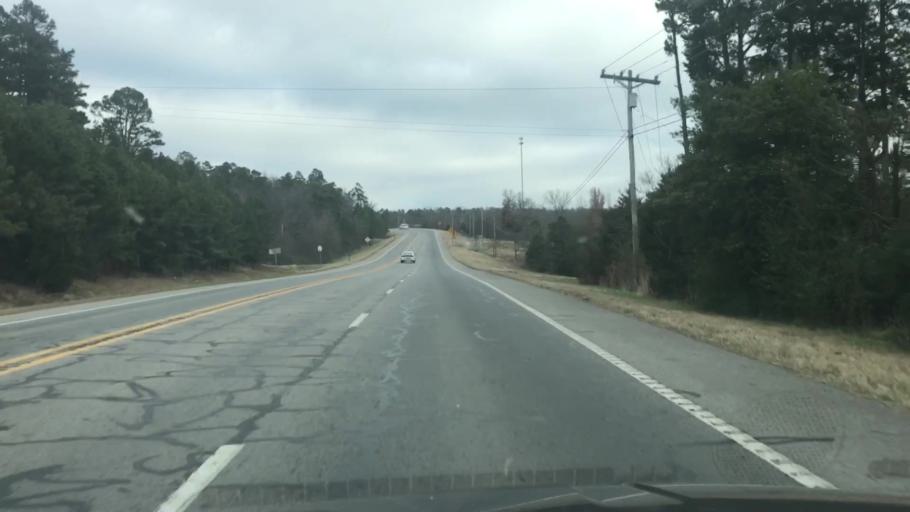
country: US
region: Arkansas
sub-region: Scott County
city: Waldron
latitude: 34.8144
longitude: -94.0395
